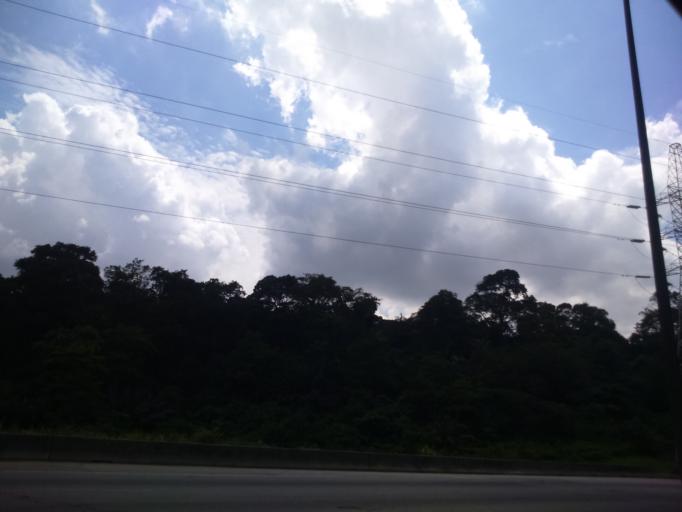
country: CI
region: Lagunes
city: Abidjan
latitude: 5.3621
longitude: -4.0369
